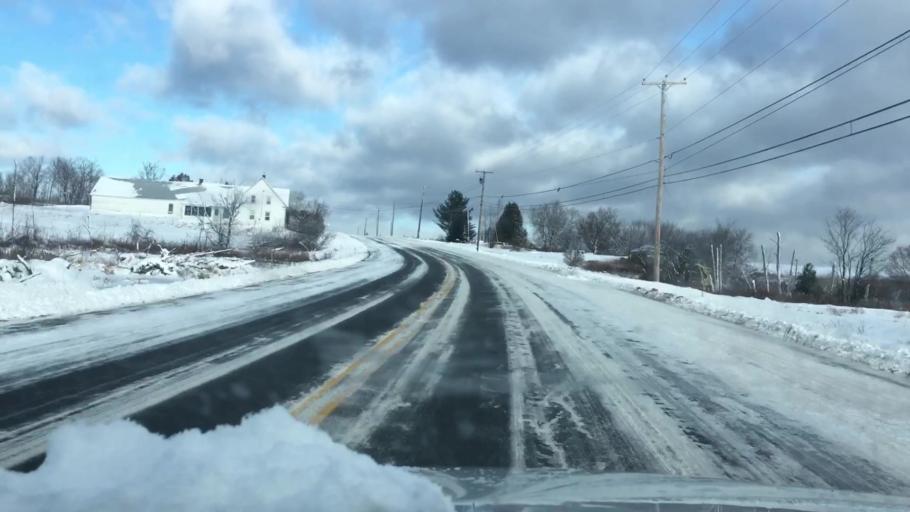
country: US
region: Maine
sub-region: Aroostook County
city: Caribou
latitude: 46.9484
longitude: -68.0230
